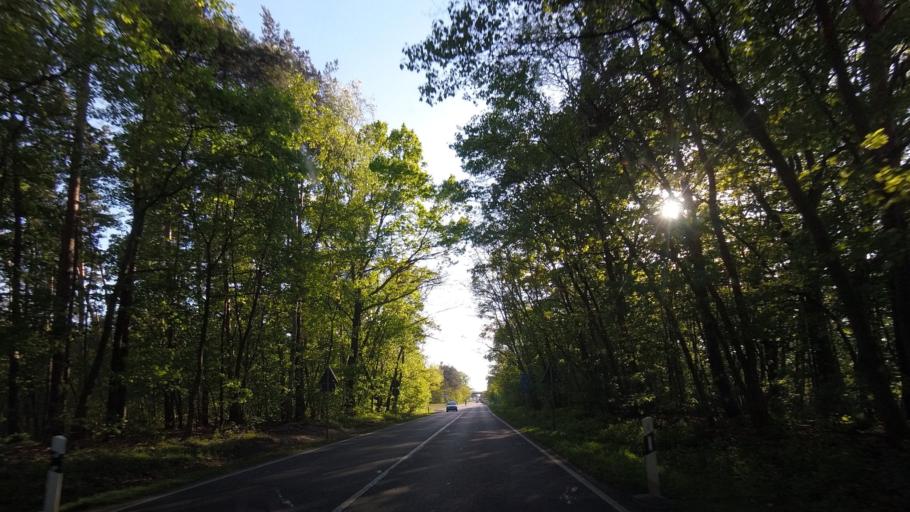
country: DE
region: Brandenburg
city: Luebben
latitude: 51.9010
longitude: 13.8200
